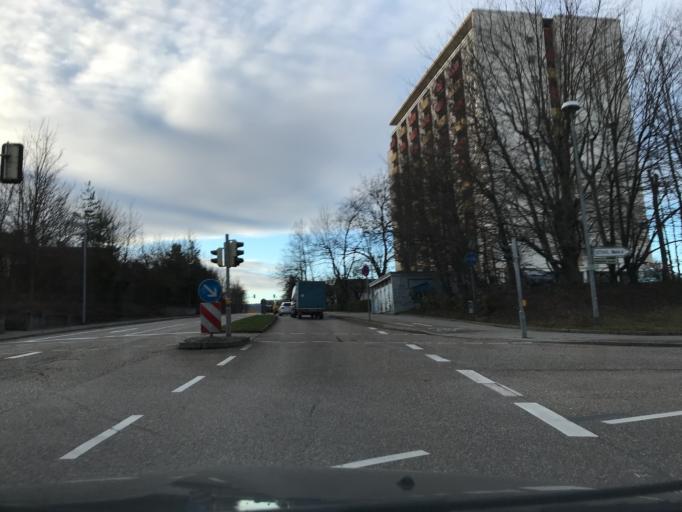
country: DE
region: Baden-Wuerttemberg
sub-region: Regierungsbezirk Stuttgart
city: Waiblingen
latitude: 48.8246
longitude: 9.3076
